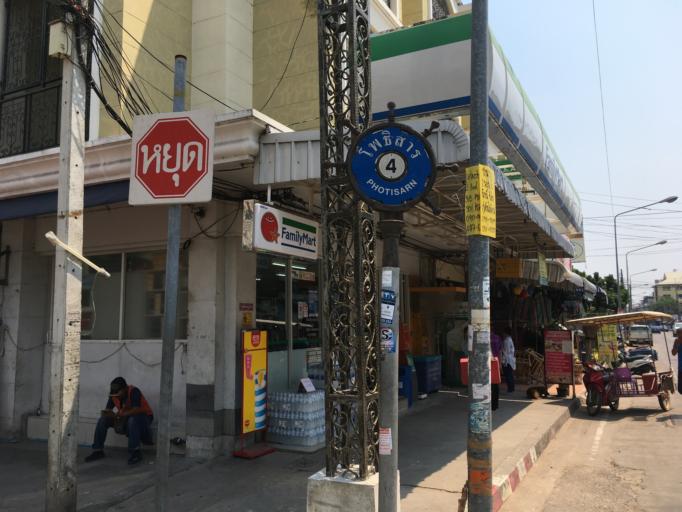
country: TH
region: Chon Buri
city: Phatthaya
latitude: 12.9542
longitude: 100.9017
